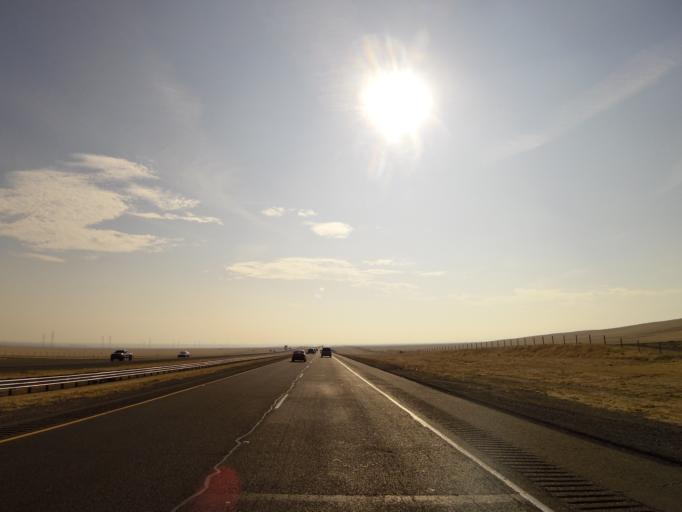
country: US
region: California
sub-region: Fresno County
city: San Joaquin
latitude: 36.4696
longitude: -120.4259
